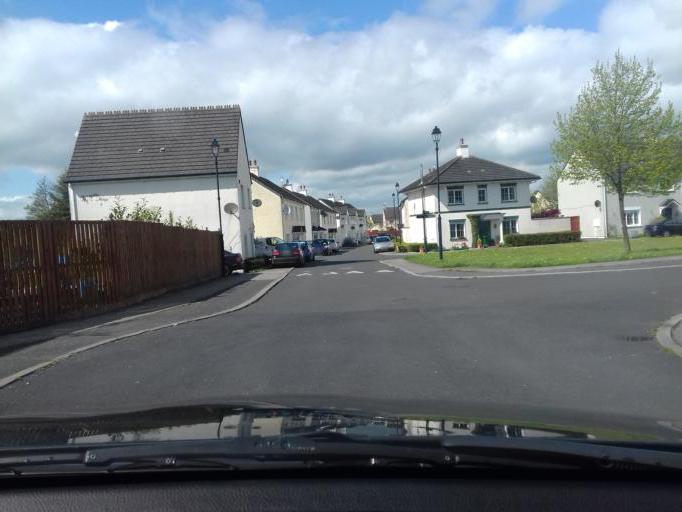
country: IE
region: Leinster
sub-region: Laois
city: Portlaoise
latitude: 53.0404
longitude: -7.2989
